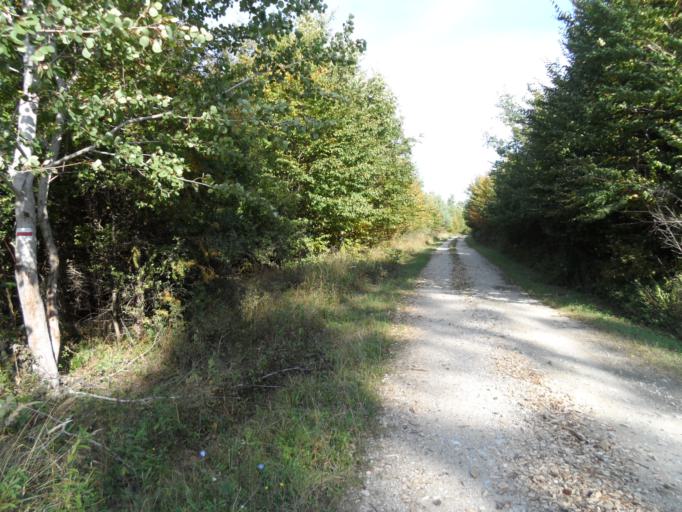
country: HU
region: Veszprem
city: Devecser
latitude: 47.2115
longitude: 17.4586
